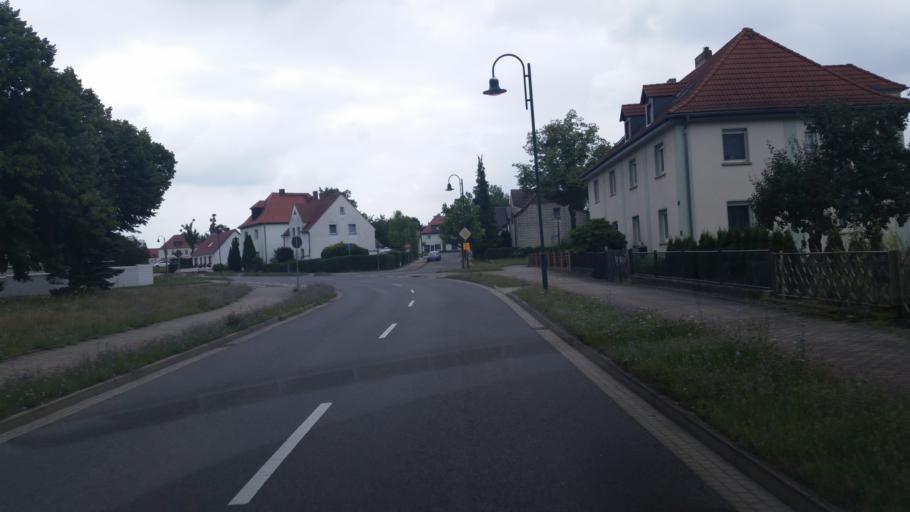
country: DE
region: Saxony
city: Bernsdorf
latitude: 51.4607
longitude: 14.0945
